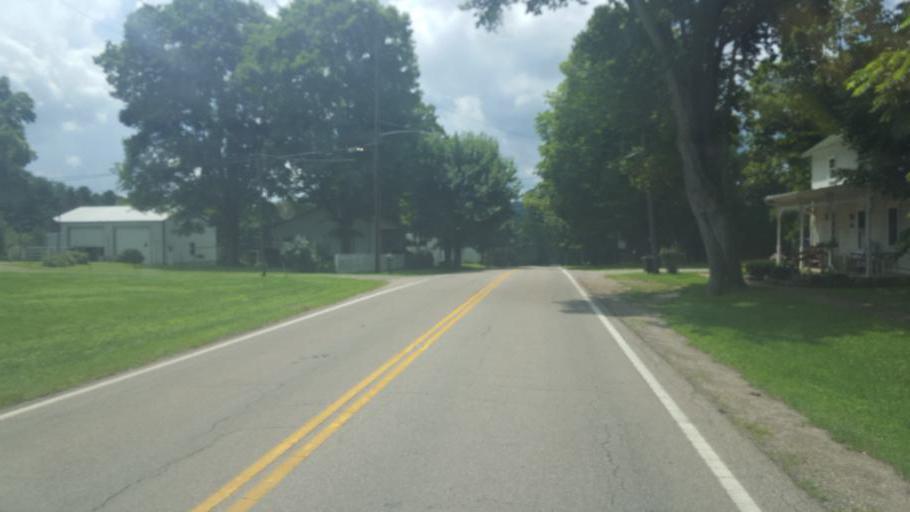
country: US
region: Ohio
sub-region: Ross County
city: Kingston
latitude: 39.4651
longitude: -82.7481
